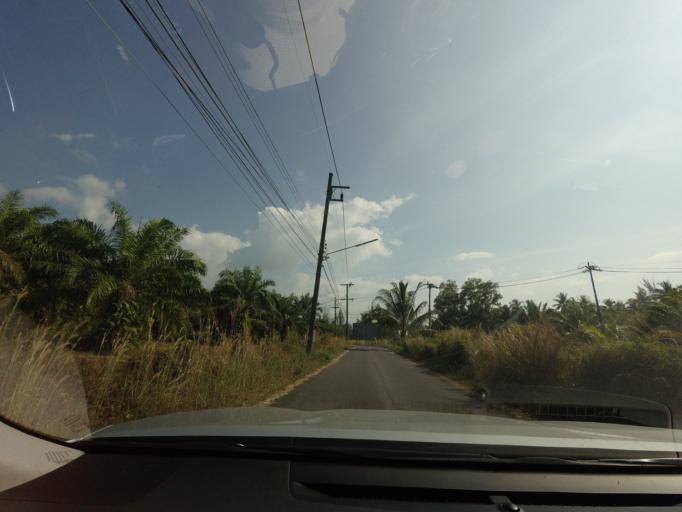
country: TH
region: Phangnga
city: Ban Khao Lak
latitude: 8.7246
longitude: 98.2436
